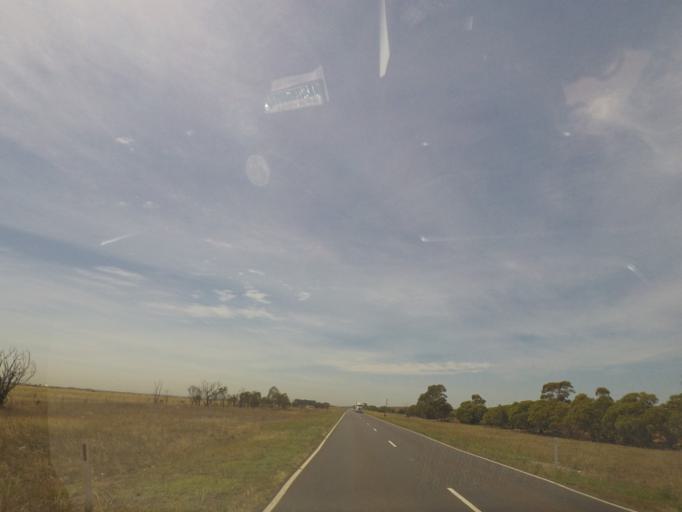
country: AU
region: Victoria
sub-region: Wyndham
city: Wyndham Vale
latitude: -37.8362
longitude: 144.5498
